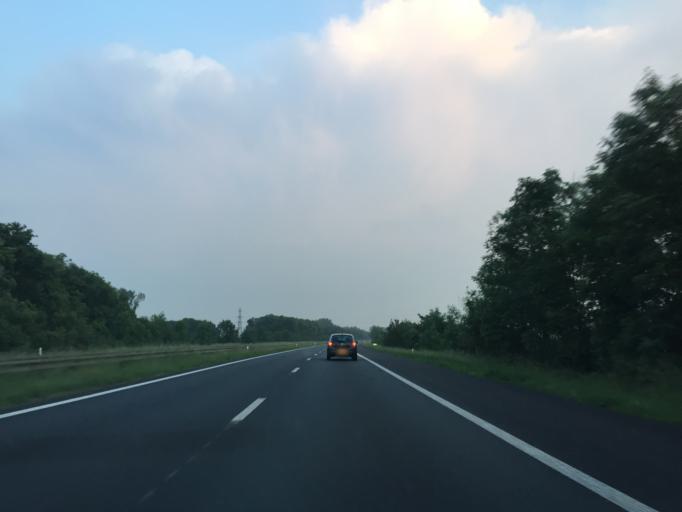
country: NL
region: Gelderland
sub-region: Gemeente Buren
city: Lienden
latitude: 51.9092
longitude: 5.4914
